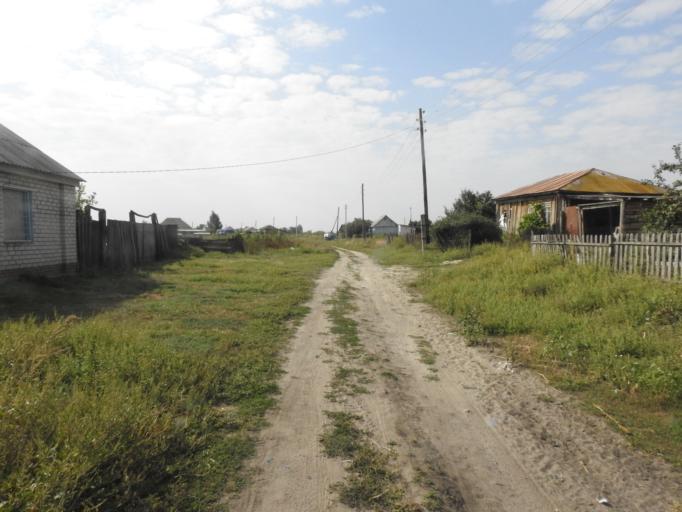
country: RU
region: Saratov
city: Lysyye Gory
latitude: 51.2514
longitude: 45.0010
